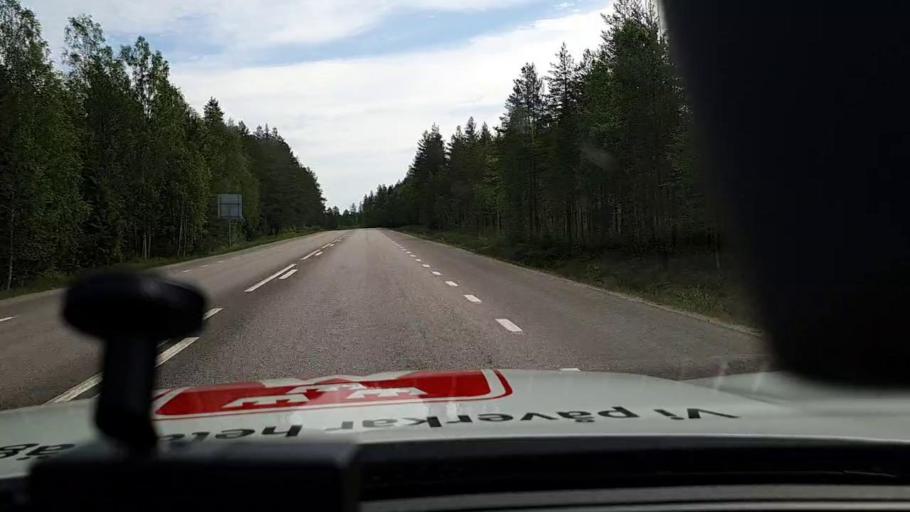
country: SE
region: Norrbotten
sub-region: Lulea Kommun
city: Gammelstad
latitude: 65.5823
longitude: 22.0055
